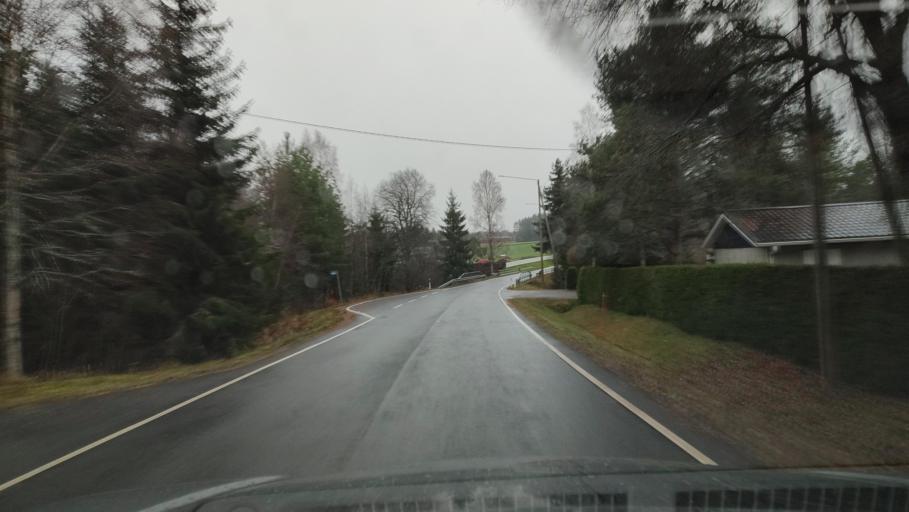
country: FI
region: Southern Ostrobothnia
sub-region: Suupohja
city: Karijoki
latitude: 62.1346
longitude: 21.6808
